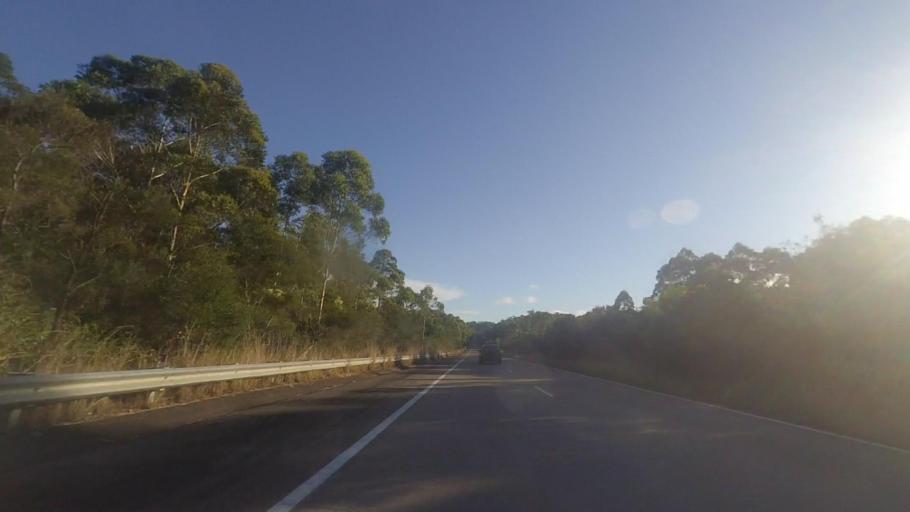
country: AU
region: New South Wales
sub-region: Great Lakes
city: Bulahdelah
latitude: -32.3049
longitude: 152.3458
